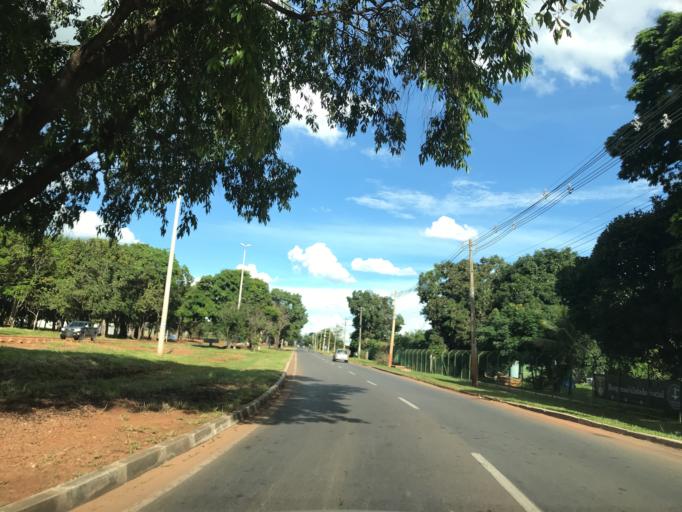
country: BR
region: Federal District
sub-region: Brasilia
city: Brasilia
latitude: -15.8170
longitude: -47.8666
